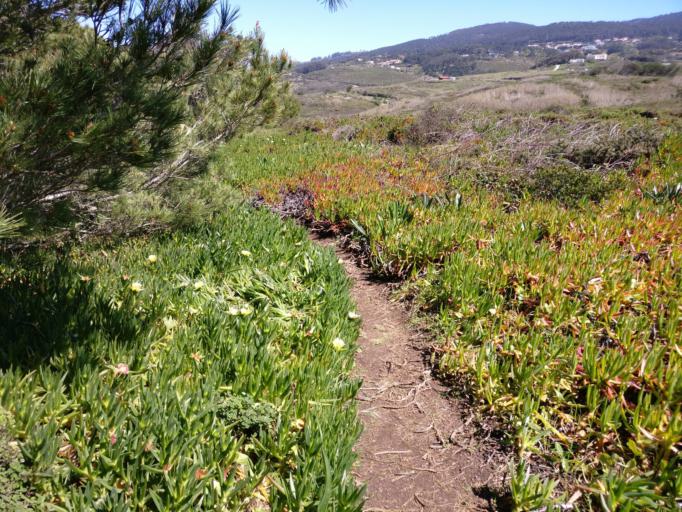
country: PT
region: Lisbon
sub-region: Sintra
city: Colares
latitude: 38.7849
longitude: -9.4931
